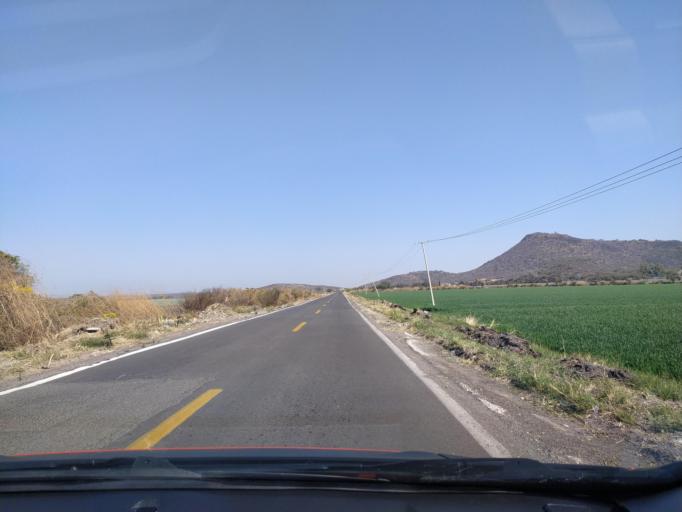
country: MX
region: Guanajuato
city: Ciudad Manuel Doblado
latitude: 20.7816
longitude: -101.8337
